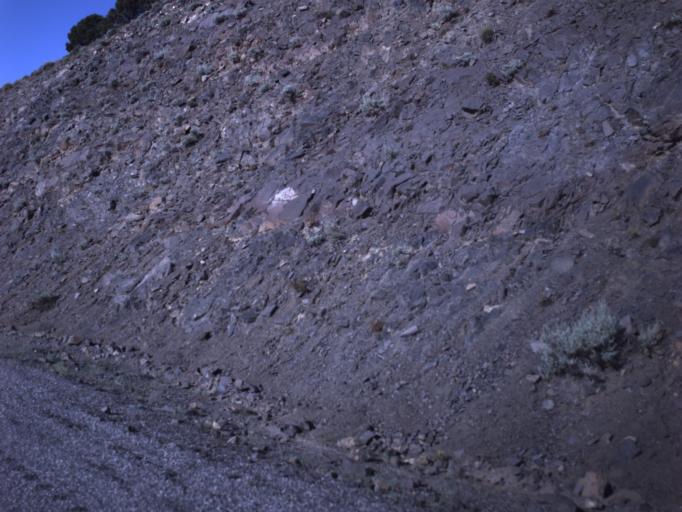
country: US
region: Utah
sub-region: Wayne County
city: Loa
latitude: 38.5892
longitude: -111.4742
